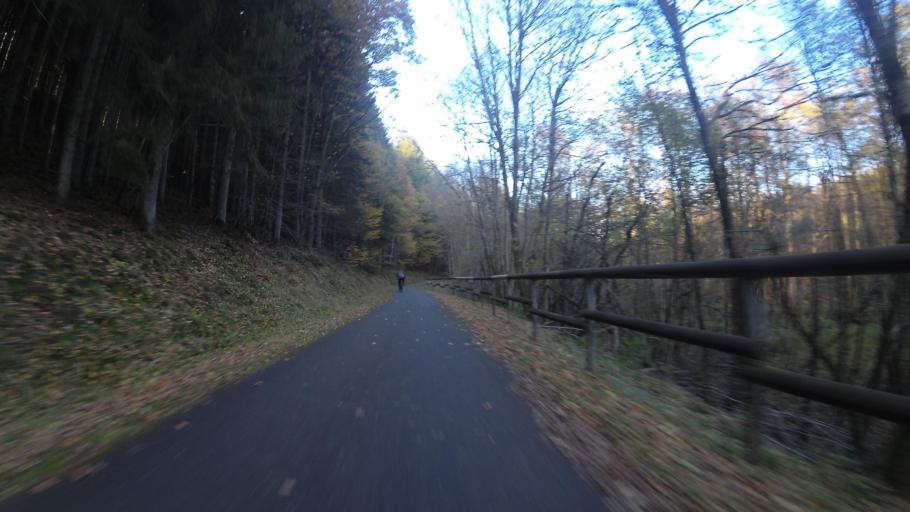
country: DE
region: Rheinland-Pfalz
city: Hentern
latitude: 49.6094
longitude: 6.7225
